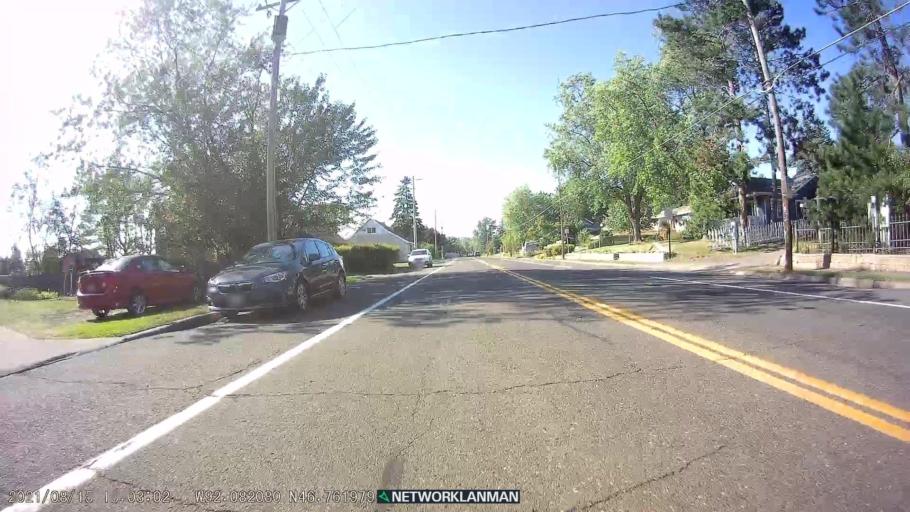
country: US
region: Minnesota
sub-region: Saint Louis County
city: Duluth
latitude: 46.7619
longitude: -92.0819
